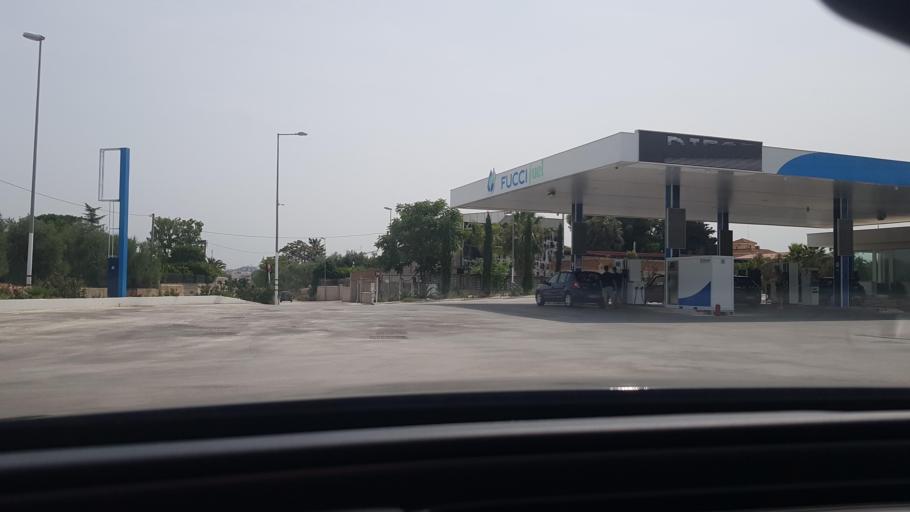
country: IT
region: Apulia
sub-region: Provincia di Barletta - Andria - Trani
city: Andria
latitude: 41.2307
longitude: 16.2747
